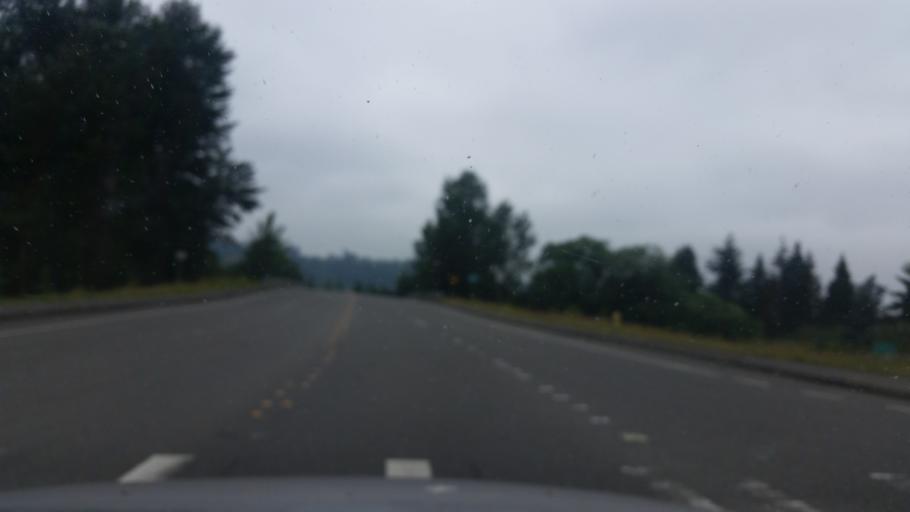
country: US
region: Washington
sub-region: Pierce County
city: Sumner
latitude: 47.2159
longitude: -122.2375
